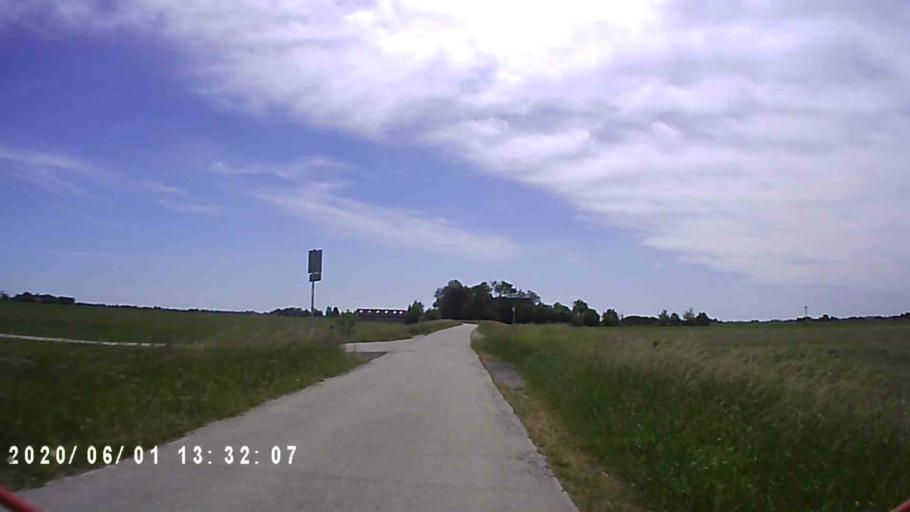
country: NL
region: Friesland
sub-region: Gemeente Littenseradiel
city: Wommels
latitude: 53.0939
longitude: 5.5675
